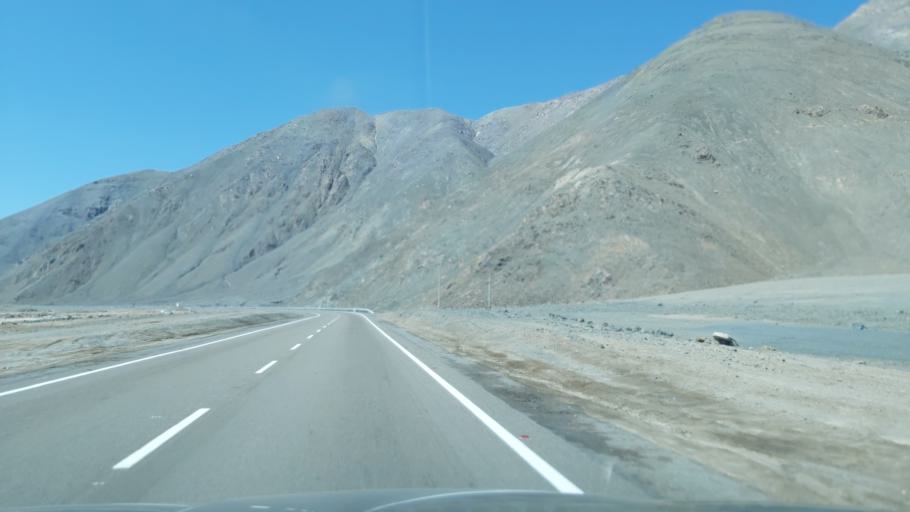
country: CL
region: Atacama
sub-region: Provincia de Chanaral
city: Diego de Almagro
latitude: -26.3464
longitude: -69.7428
